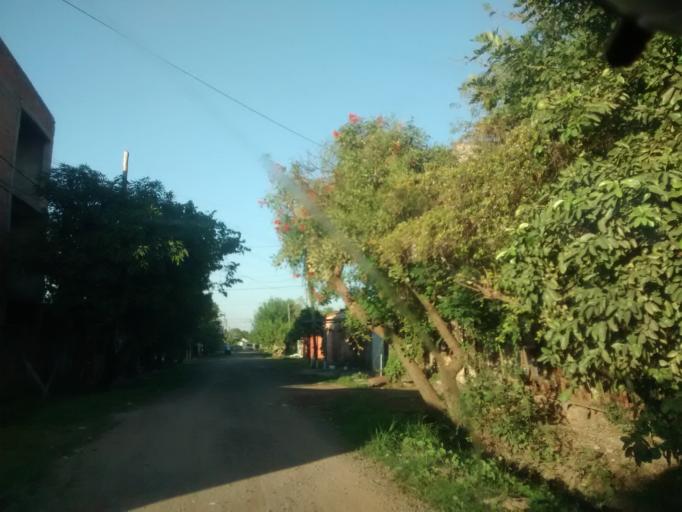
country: AR
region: Chaco
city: Resistencia
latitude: -27.4662
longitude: -58.9800
